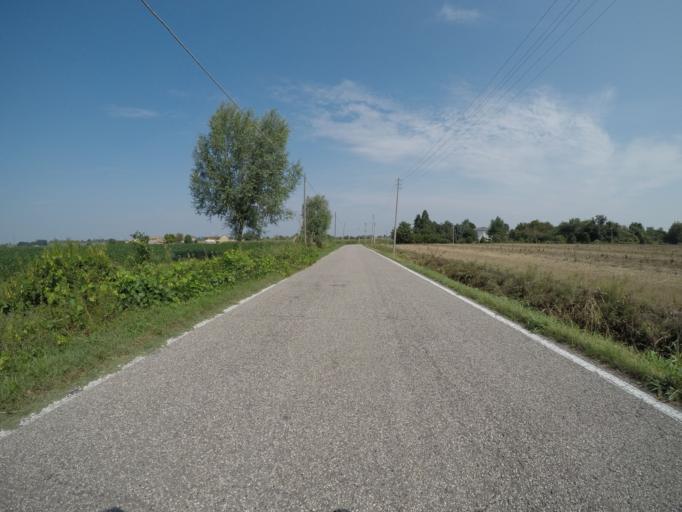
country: IT
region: Veneto
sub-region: Provincia di Rovigo
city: Lendinara
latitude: 45.1095
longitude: 11.5970
